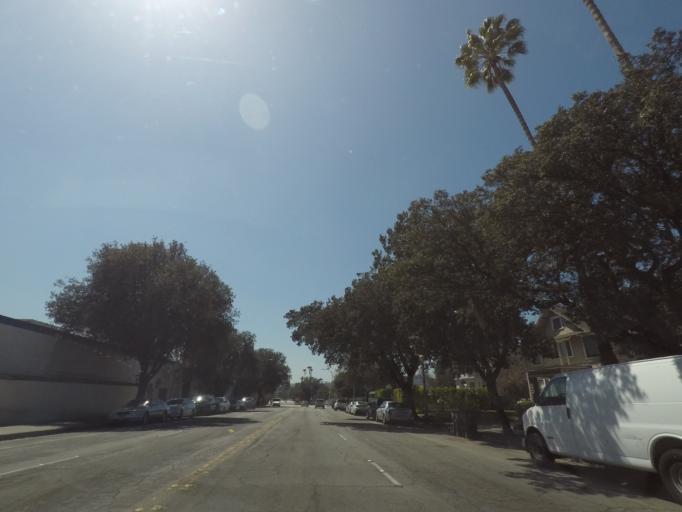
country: US
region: California
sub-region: Los Angeles County
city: Pasadena
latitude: 34.1565
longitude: -118.1535
